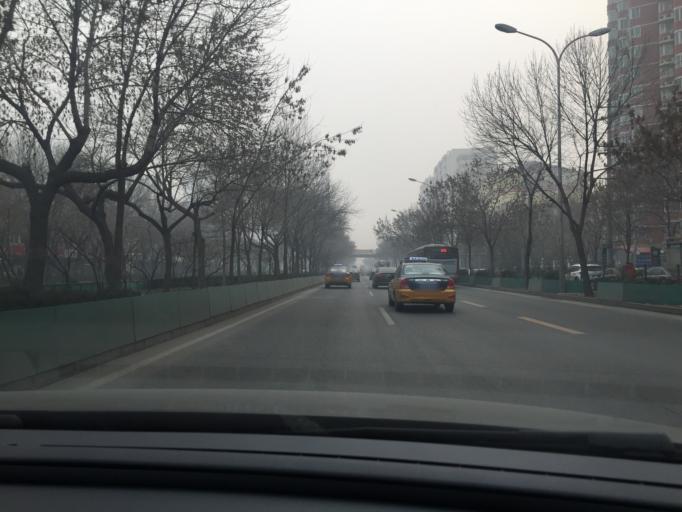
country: CN
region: Beijing
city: Qinghe
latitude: 40.0052
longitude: 116.3461
